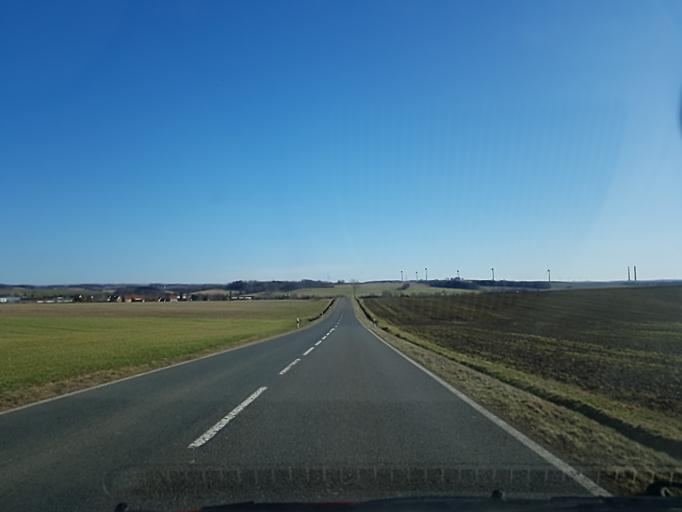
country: DE
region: Saxony
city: Niederschona
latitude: 50.9481
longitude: 13.4184
